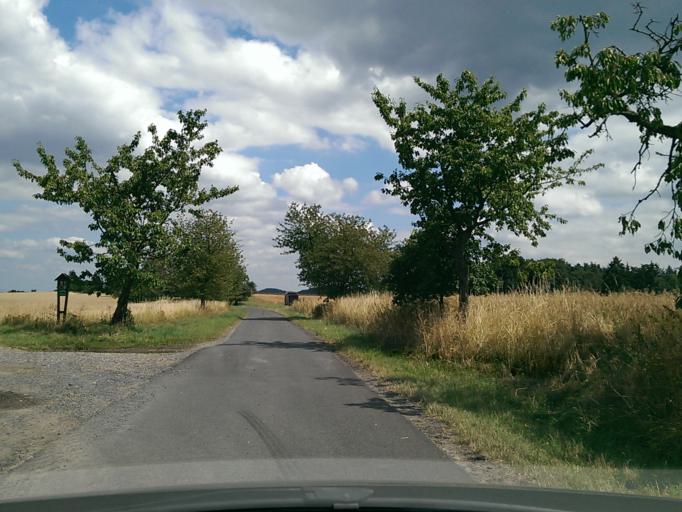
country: CZ
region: Ustecky
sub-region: Okres Litomerice
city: Steti
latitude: 50.5145
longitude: 14.4473
